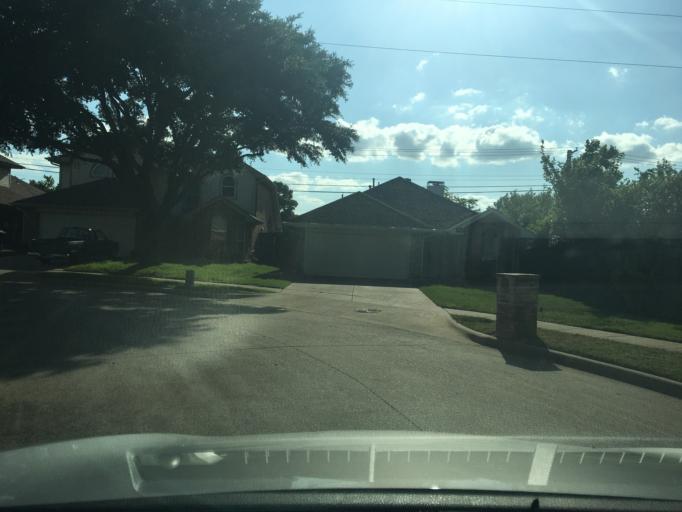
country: US
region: Texas
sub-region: Dallas County
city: Richardson
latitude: 32.9369
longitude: -96.6821
